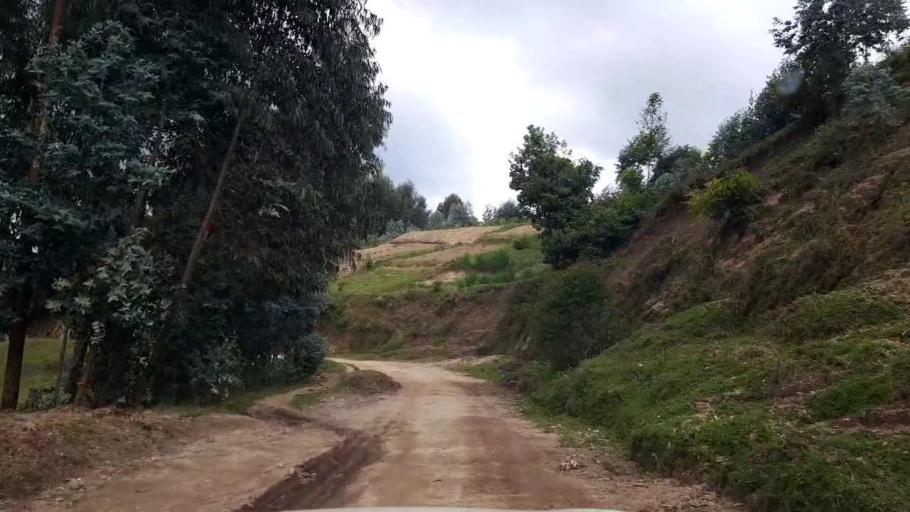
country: RW
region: Western Province
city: Kibuye
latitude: -1.8658
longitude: 29.5492
